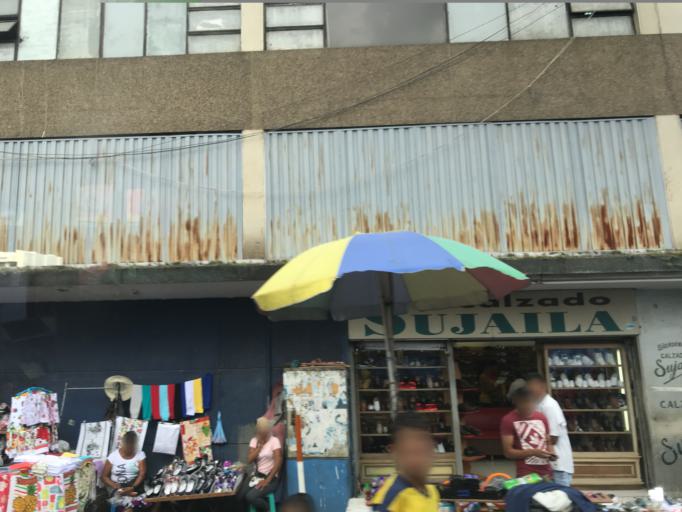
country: CO
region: Valle del Cauca
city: Cali
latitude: 3.4494
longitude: -76.5305
